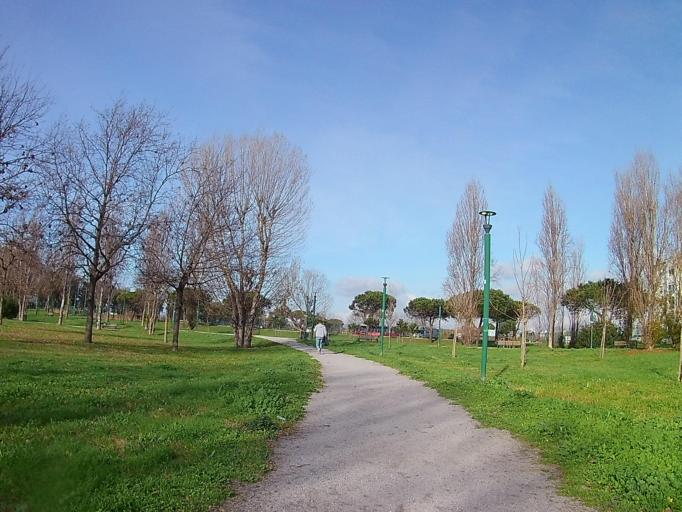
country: IT
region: Latium
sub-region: Citta metropolitana di Roma Capitale
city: Lido di Ostia
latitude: 41.7418
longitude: 12.2628
